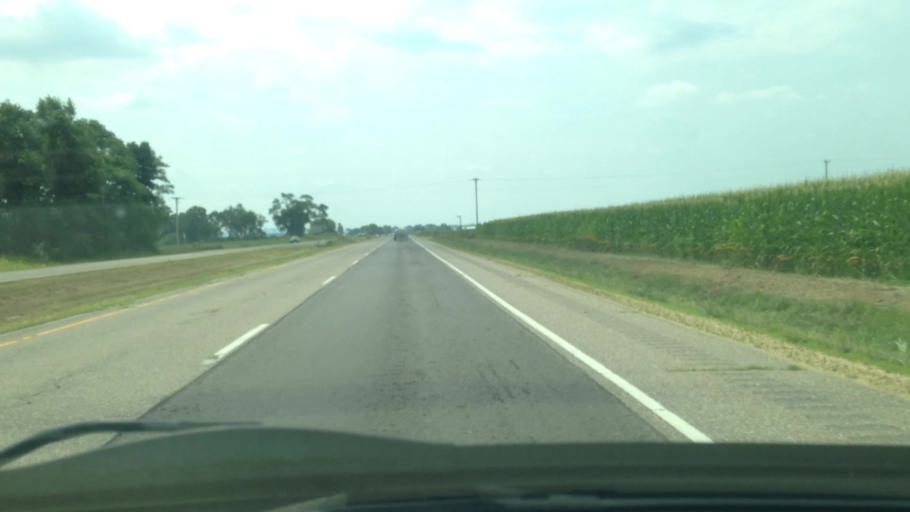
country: US
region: Wisconsin
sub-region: Sauk County
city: Prairie du Sac
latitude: 43.3419
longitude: -89.7590
